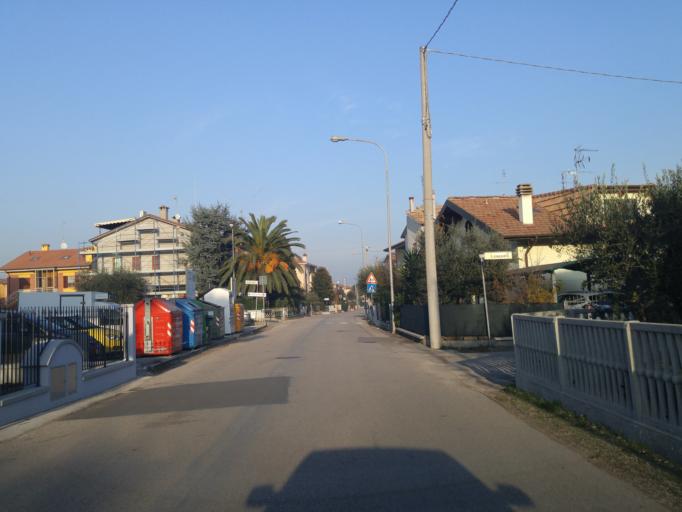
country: IT
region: The Marches
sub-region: Provincia di Pesaro e Urbino
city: Rosciano
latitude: 43.8263
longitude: 13.0078
